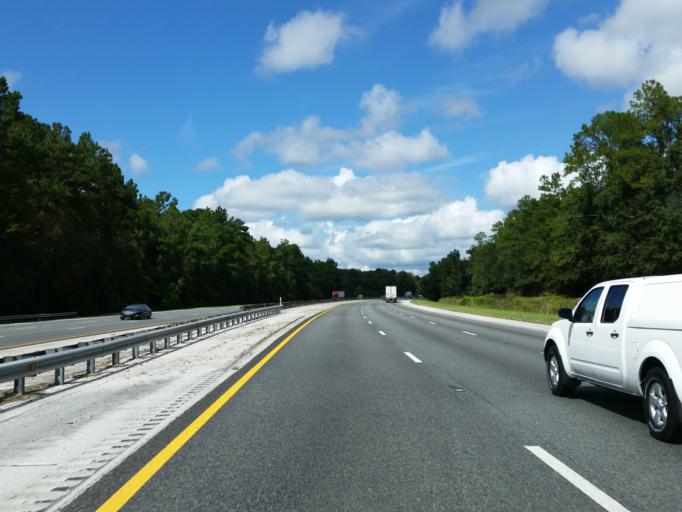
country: US
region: Florida
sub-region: Marion County
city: Citra
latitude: 29.4248
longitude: -82.2607
